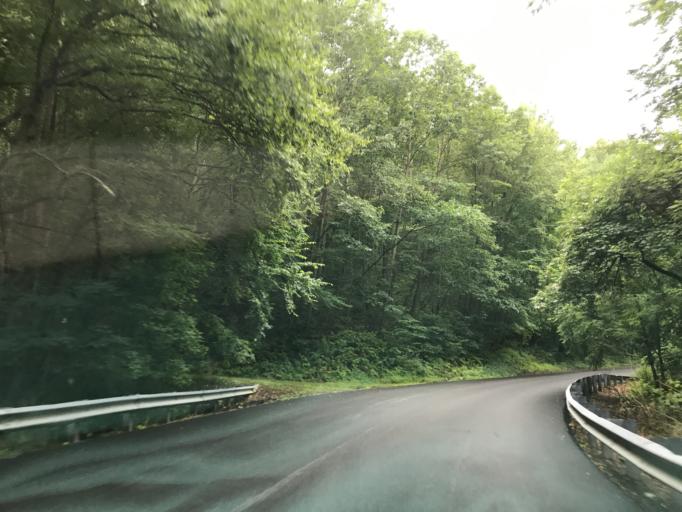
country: US
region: Pennsylvania
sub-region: York County
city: New Freedom
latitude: 39.6797
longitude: -76.7709
